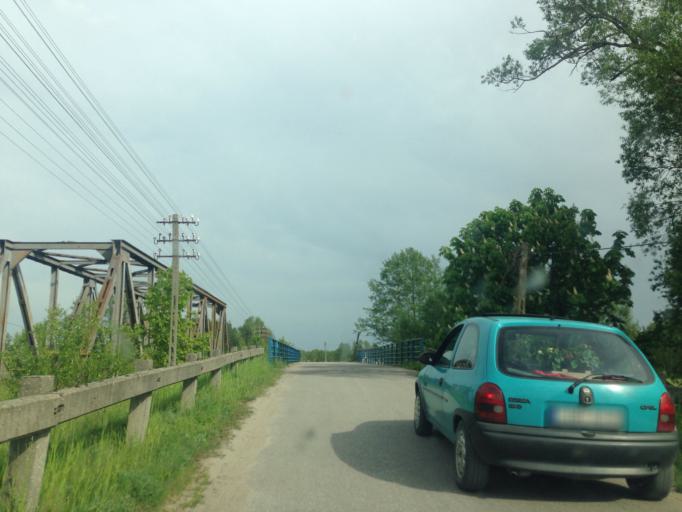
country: PL
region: Kujawsko-Pomorskie
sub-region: Powiat brodnicki
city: Brodnica
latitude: 53.2798
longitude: 19.4783
